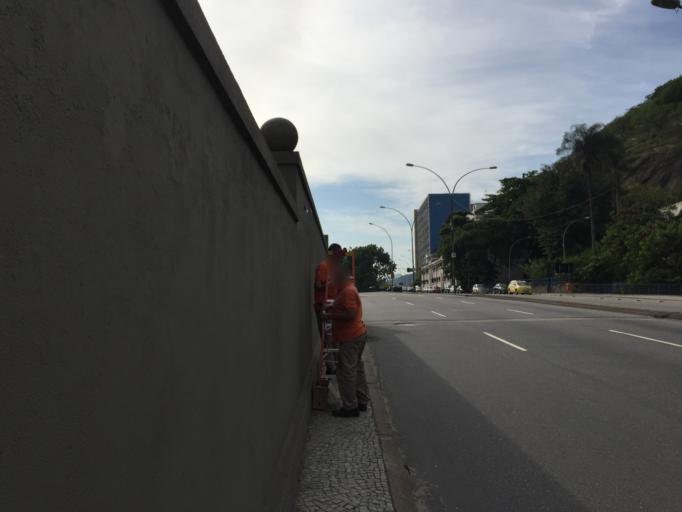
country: BR
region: Rio de Janeiro
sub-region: Rio De Janeiro
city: Rio de Janeiro
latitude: -22.9509
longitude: -43.1803
